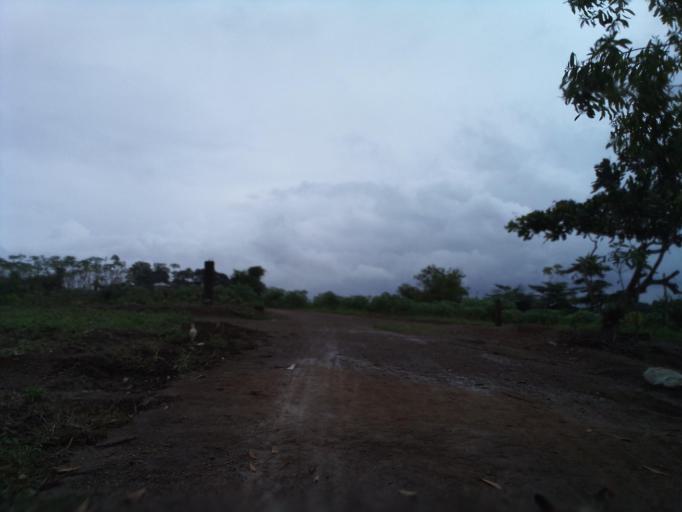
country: SL
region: Eastern Province
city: Kenema
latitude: 7.8810
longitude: -11.1628
